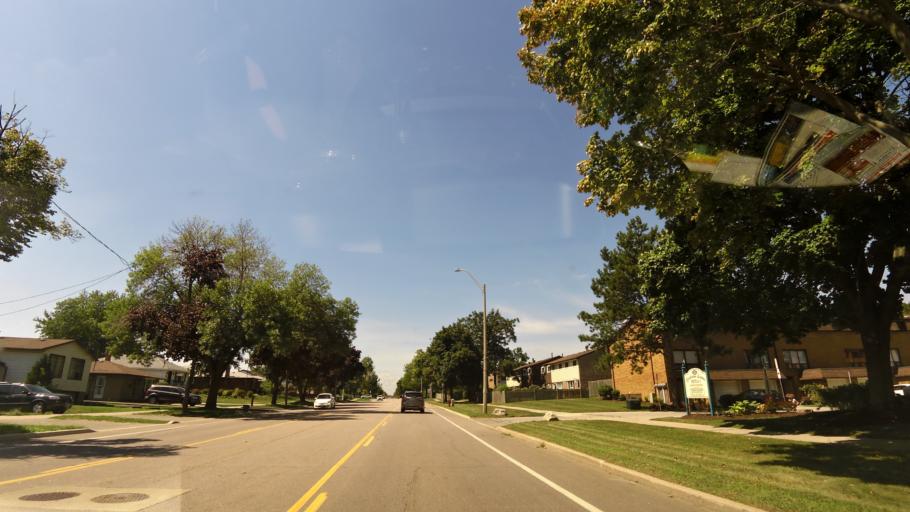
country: CA
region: Ontario
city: Hamilton
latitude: 43.2168
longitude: -79.9120
